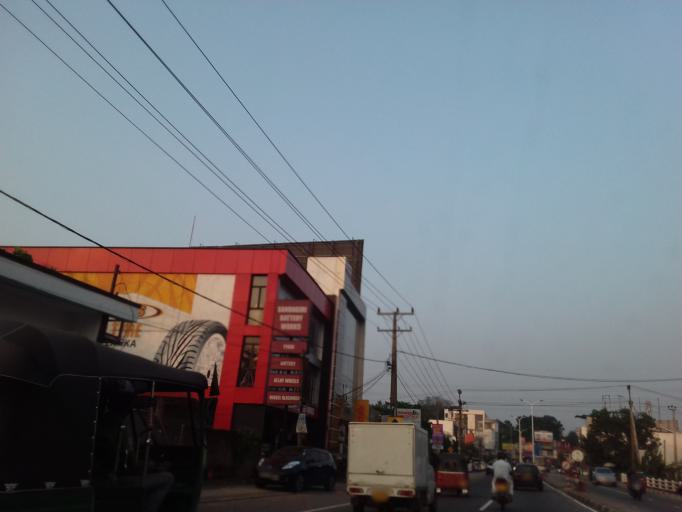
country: LK
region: Western
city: Kelaniya
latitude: 6.9852
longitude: 79.9340
